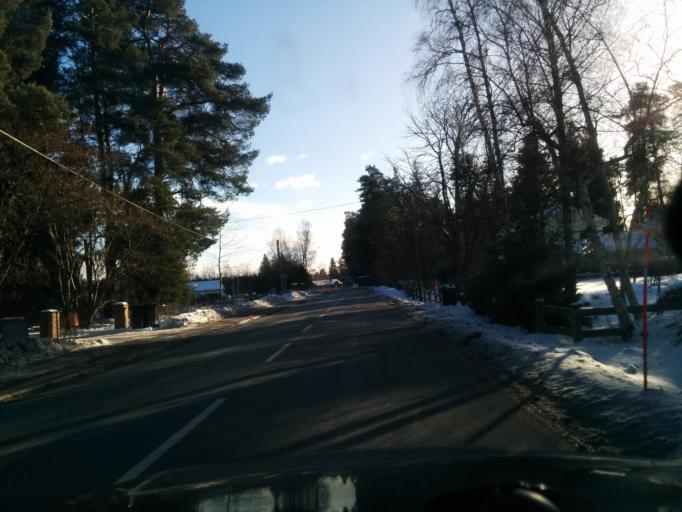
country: SE
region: Stockholm
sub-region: Taby Kommun
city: Taby
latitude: 59.4749
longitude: 18.0959
